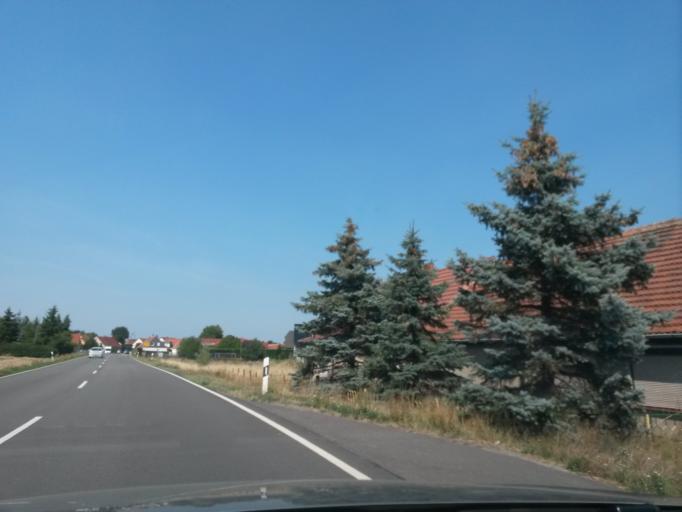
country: DE
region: Saxony-Anhalt
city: Jerichow
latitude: 52.5346
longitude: 12.0160
